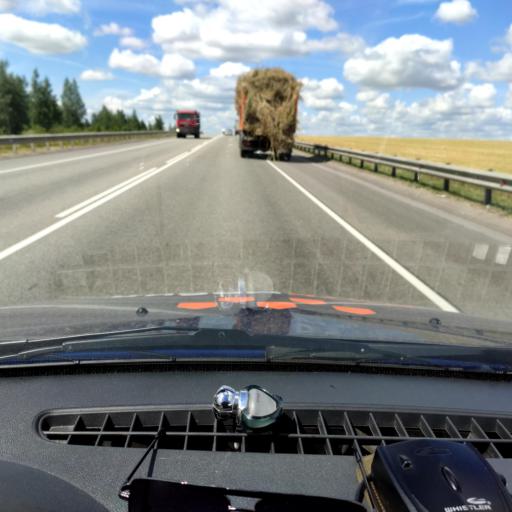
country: RU
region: Lipetsk
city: Borinskoye
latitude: 52.4737
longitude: 39.3862
